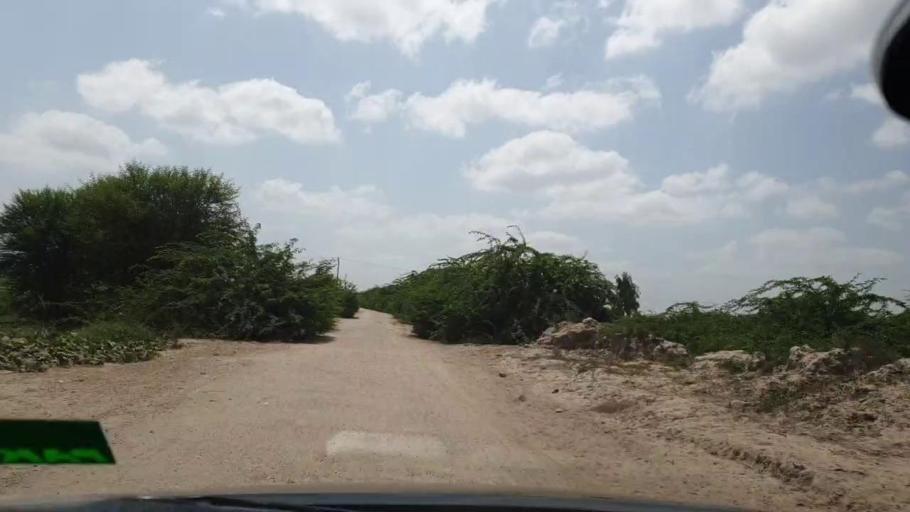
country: PK
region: Sindh
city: Kadhan
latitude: 24.5666
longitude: 69.2110
